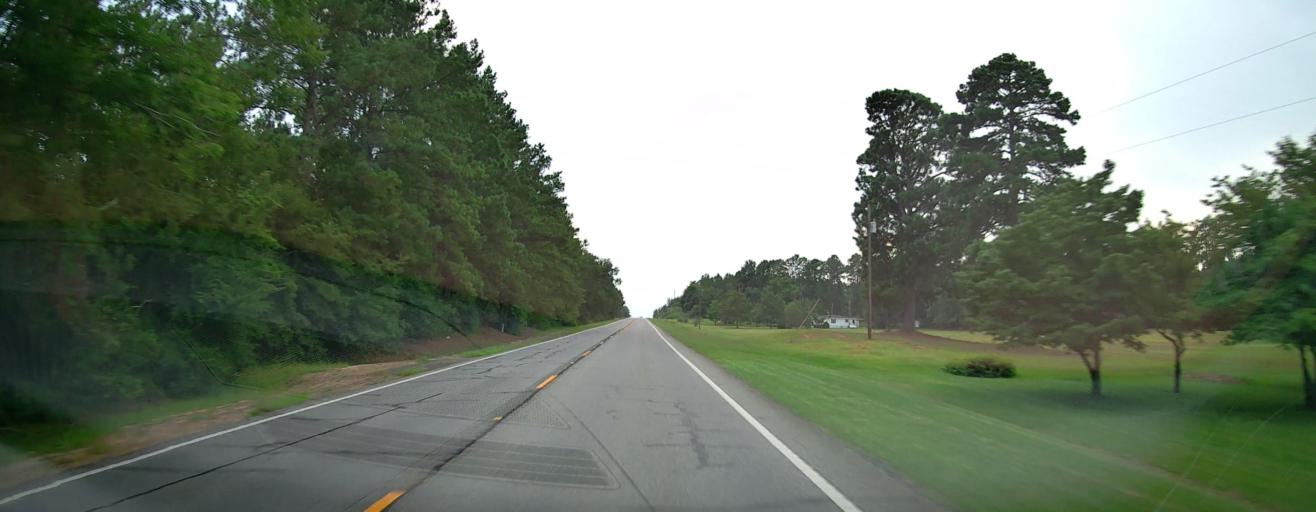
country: US
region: Georgia
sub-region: Laurens County
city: East Dublin
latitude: 32.6281
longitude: -82.8095
